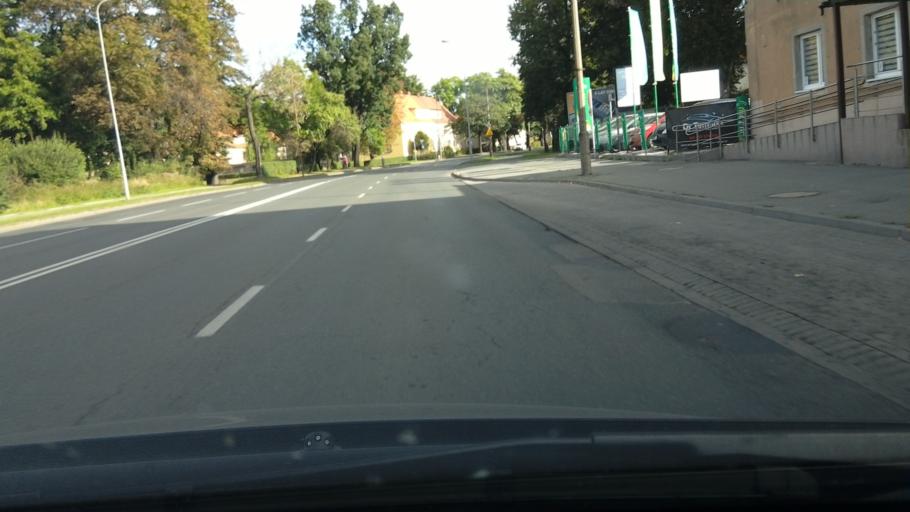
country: PL
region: Lower Silesian Voivodeship
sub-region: Jelenia Gora
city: Jelenia Gora
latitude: 50.8887
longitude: 15.7200
